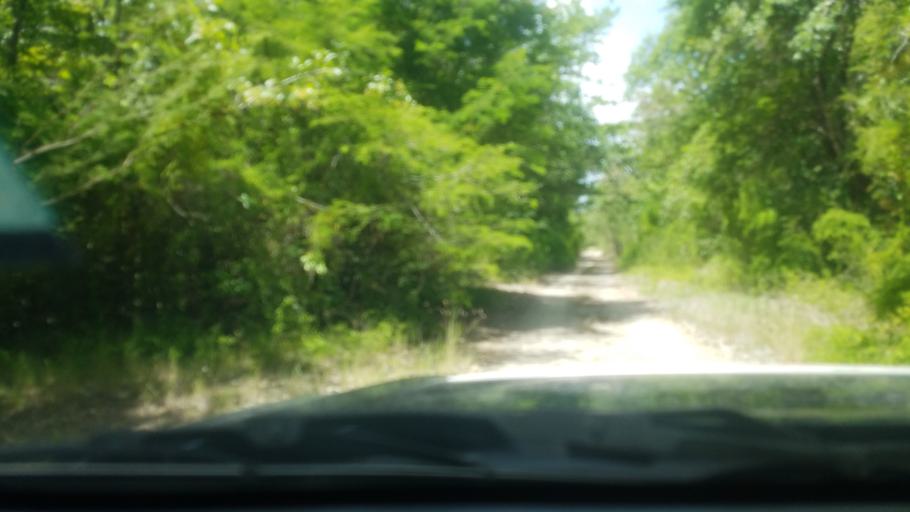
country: LC
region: Vieux-Fort
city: Vieux Fort
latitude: 13.7467
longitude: -60.9381
